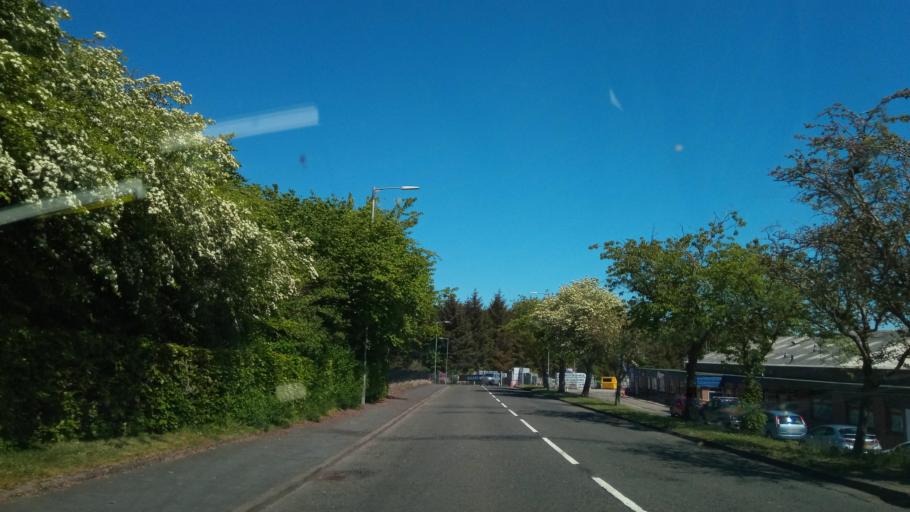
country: GB
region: Scotland
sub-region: The Scottish Borders
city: Hawick
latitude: 55.4358
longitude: -2.7604
